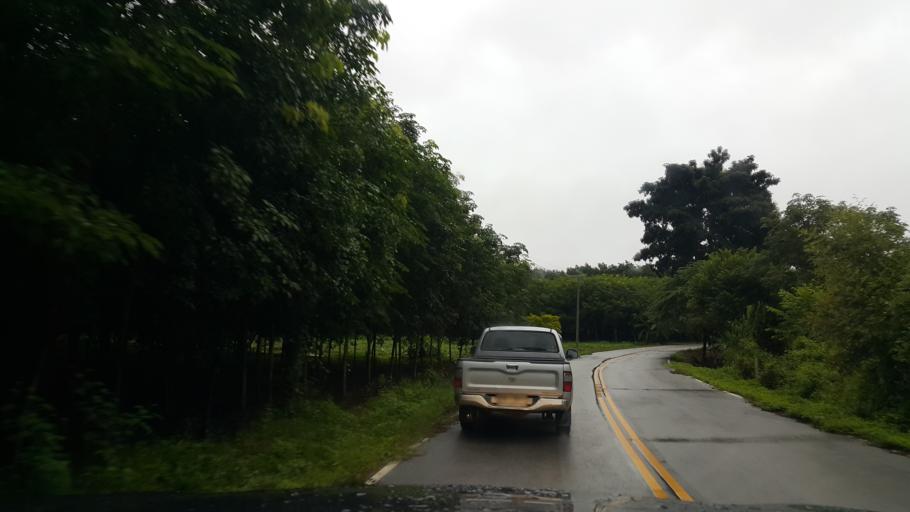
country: TH
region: Phayao
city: Phu Sang
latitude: 19.6077
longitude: 100.4074
